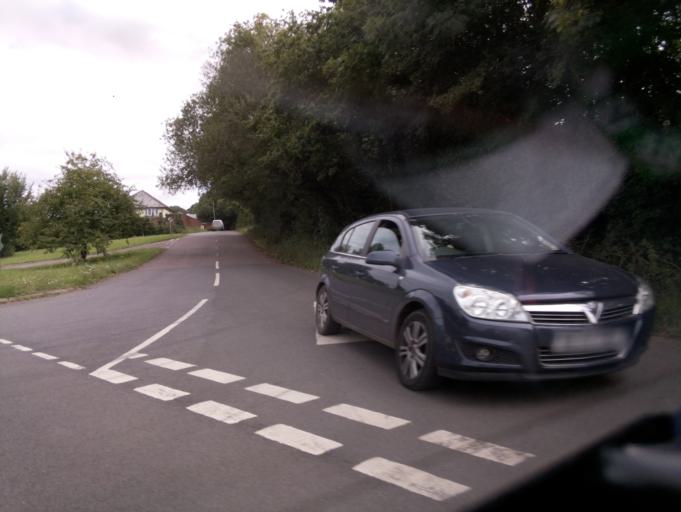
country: GB
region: England
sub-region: Devon
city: Bradninch
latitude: 50.8104
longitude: -3.4223
